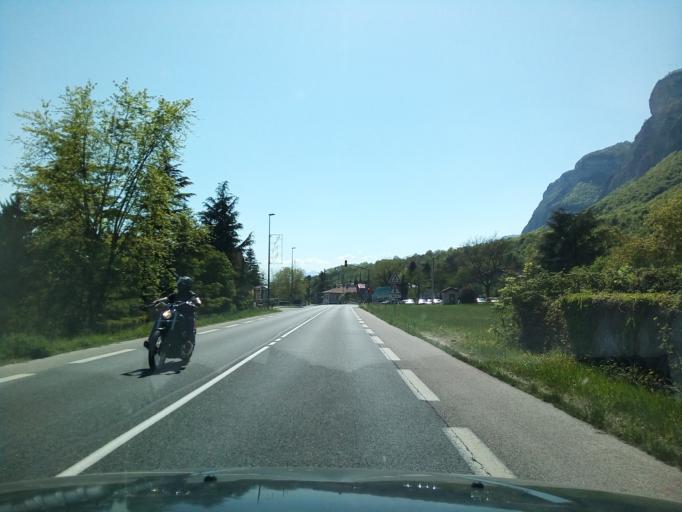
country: FR
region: Rhone-Alpes
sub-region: Departement de l'Isere
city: Lumbin
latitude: 45.2994
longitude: 5.9004
